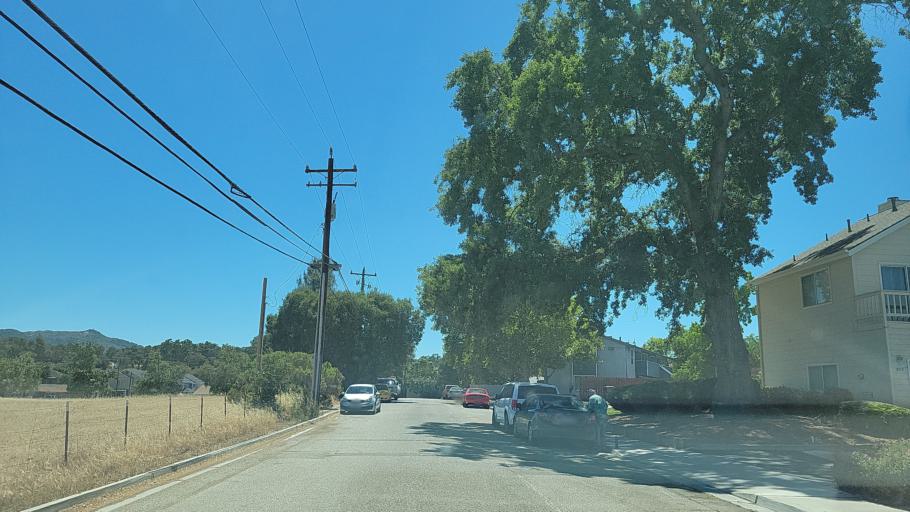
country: US
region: California
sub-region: San Luis Obispo County
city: Atascadero
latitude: 35.4622
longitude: -120.6431
